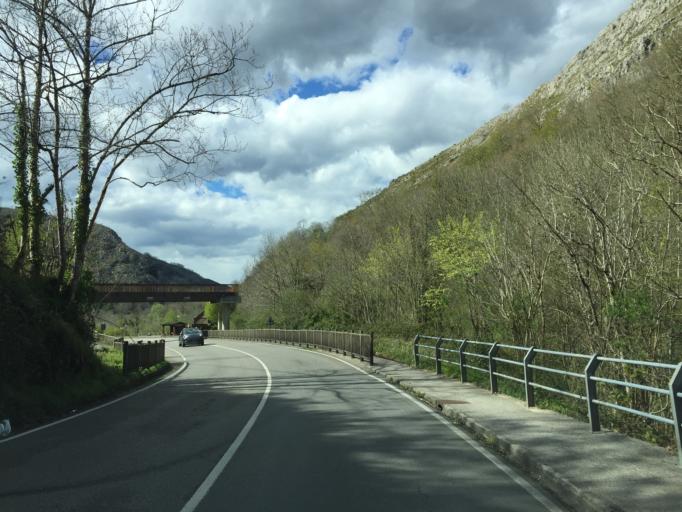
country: ES
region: Asturias
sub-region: Province of Asturias
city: Amieva
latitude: 43.3142
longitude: -5.0672
